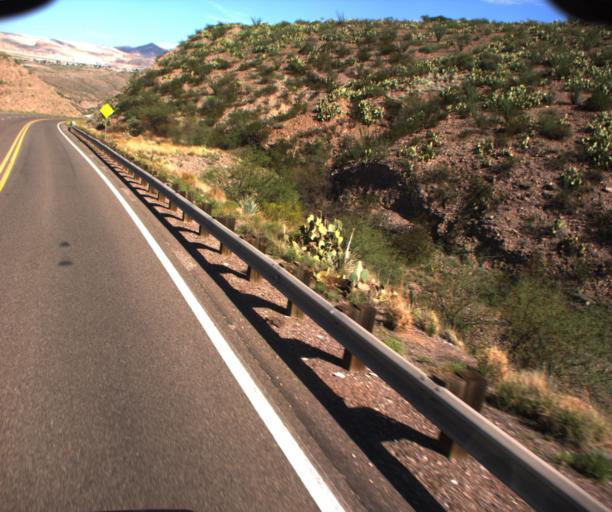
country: US
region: Arizona
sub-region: Greenlee County
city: Clifton
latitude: 33.0192
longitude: -109.2886
